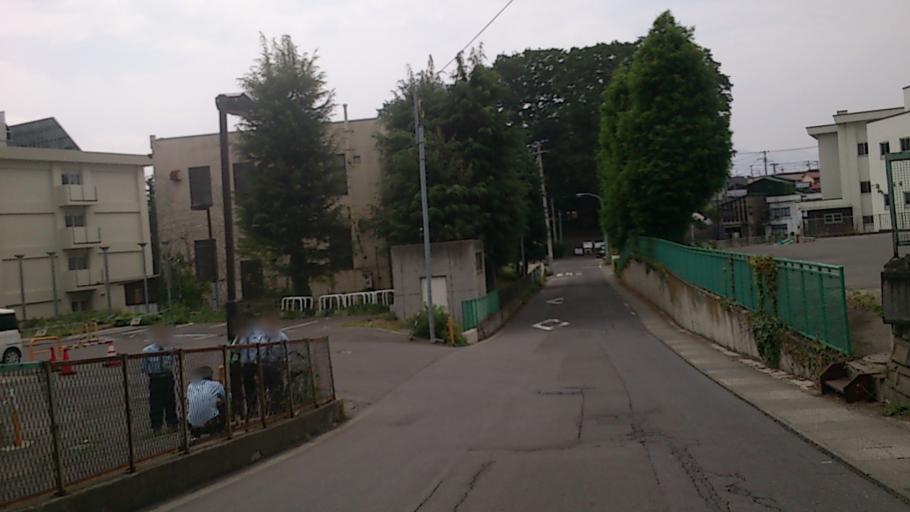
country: JP
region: Aomori
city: Hirosaki
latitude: 40.5991
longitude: 140.4650
